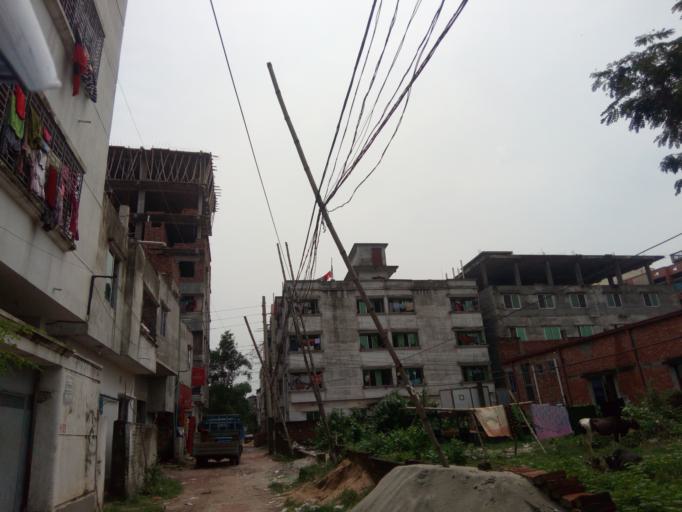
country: BD
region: Dhaka
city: Azimpur
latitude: 23.7448
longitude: 90.3495
